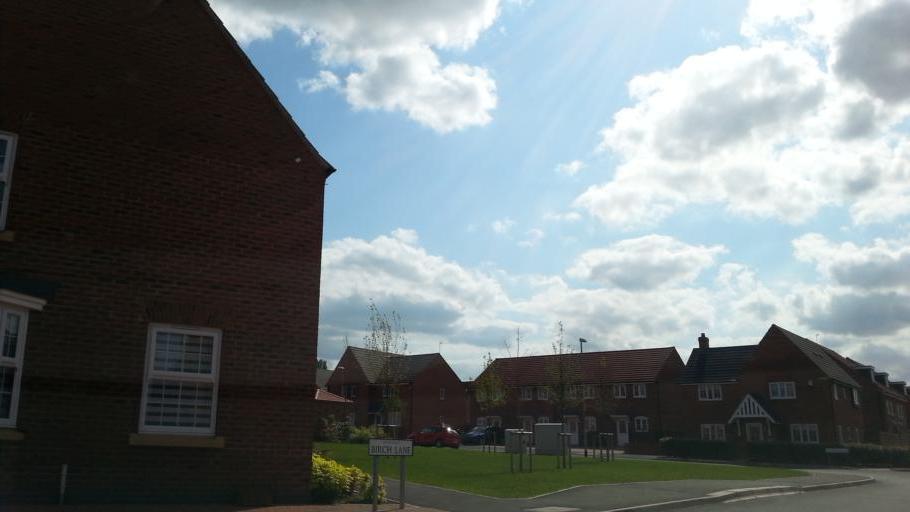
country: GB
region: England
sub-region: Leicestershire
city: Glenfield
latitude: 52.6452
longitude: -1.2120
